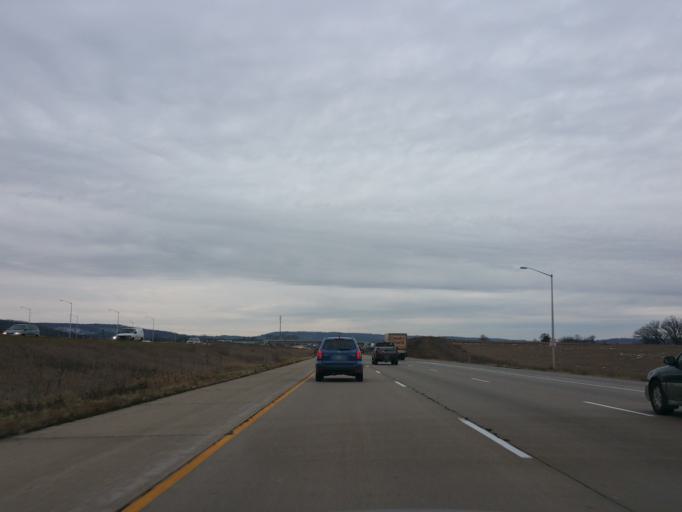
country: US
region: Wisconsin
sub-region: Columbia County
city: Poynette
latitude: 43.4257
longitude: -89.4790
